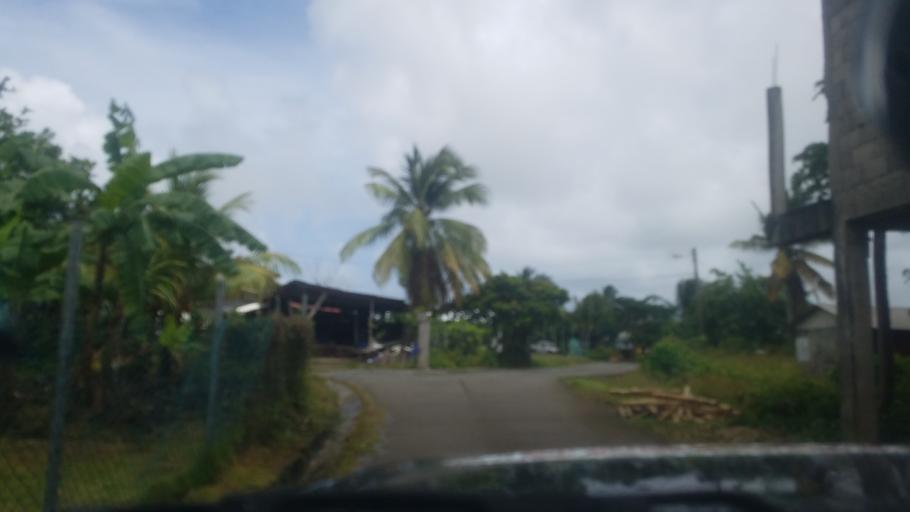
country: LC
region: Laborie Quarter
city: Laborie
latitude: 13.7577
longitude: -60.9771
